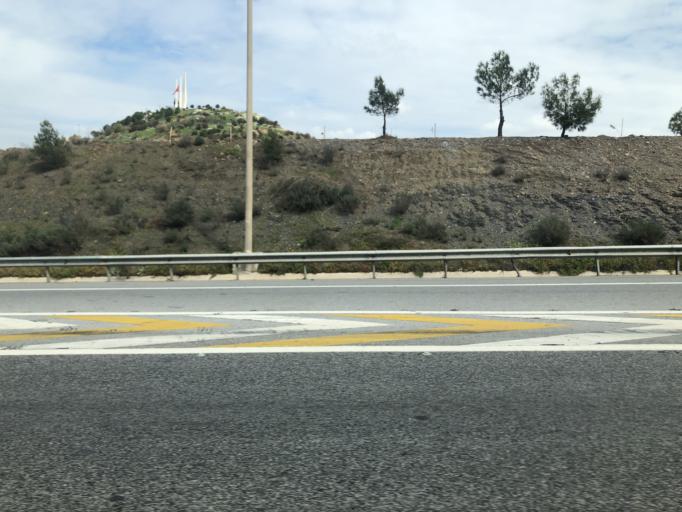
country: TR
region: Izmir
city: Karabaglar
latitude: 38.3874
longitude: 27.0660
